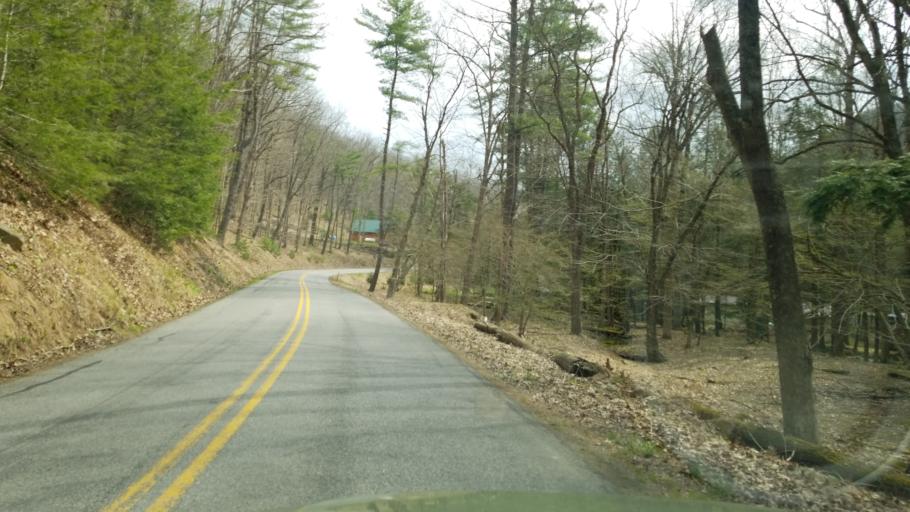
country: US
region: Pennsylvania
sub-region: Cameron County
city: Emporium
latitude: 41.2953
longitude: -78.1128
